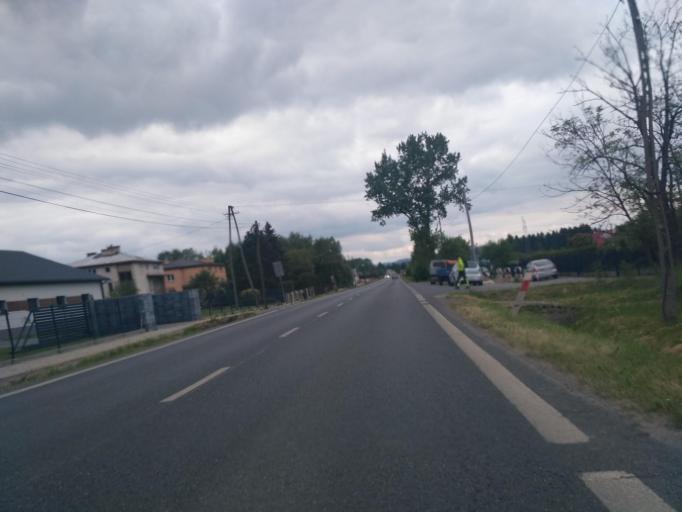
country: PL
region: Subcarpathian Voivodeship
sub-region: Powiat krosnienski
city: Odrzykon
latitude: 49.7263
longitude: 21.7131
